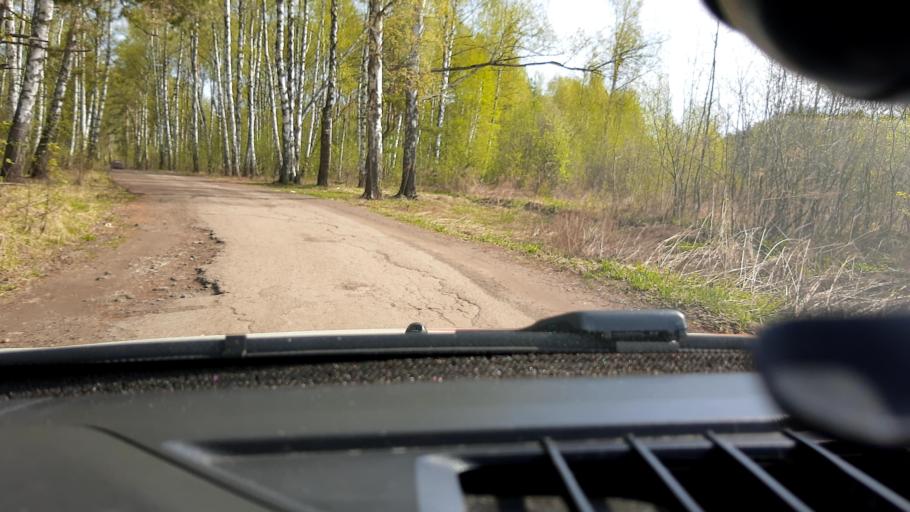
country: RU
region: Nizjnij Novgorod
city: Gorbatovka
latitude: 56.2815
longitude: 43.8004
